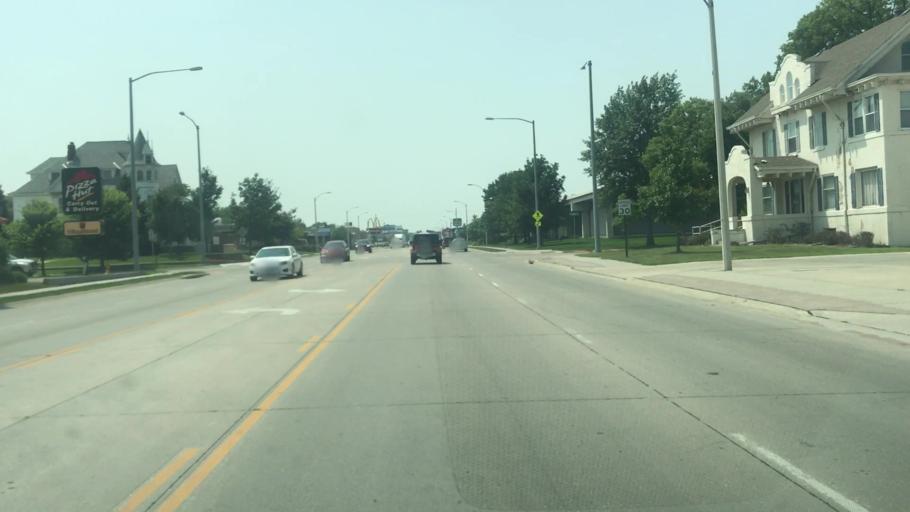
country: US
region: Nebraska
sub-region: Hall County
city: Grand Island
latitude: 40.9208
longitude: -98.3497
